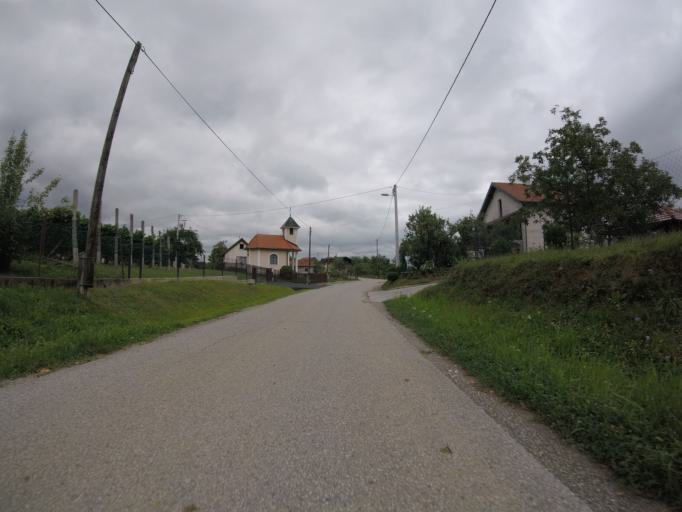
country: HR
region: Zagrebacka
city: Mraclin
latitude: 45.6032
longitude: 16.0832
